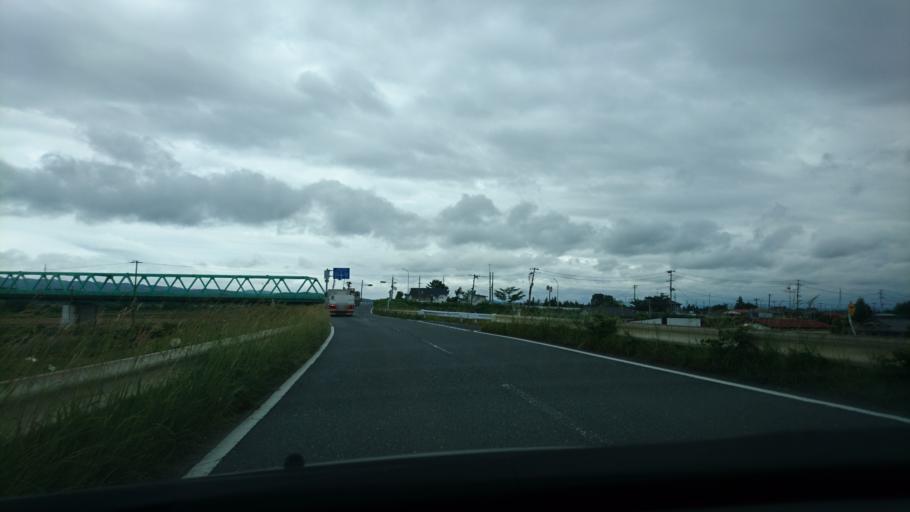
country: JP
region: Miyagi
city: Wakuya
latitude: 38.7250
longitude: 141.2631
